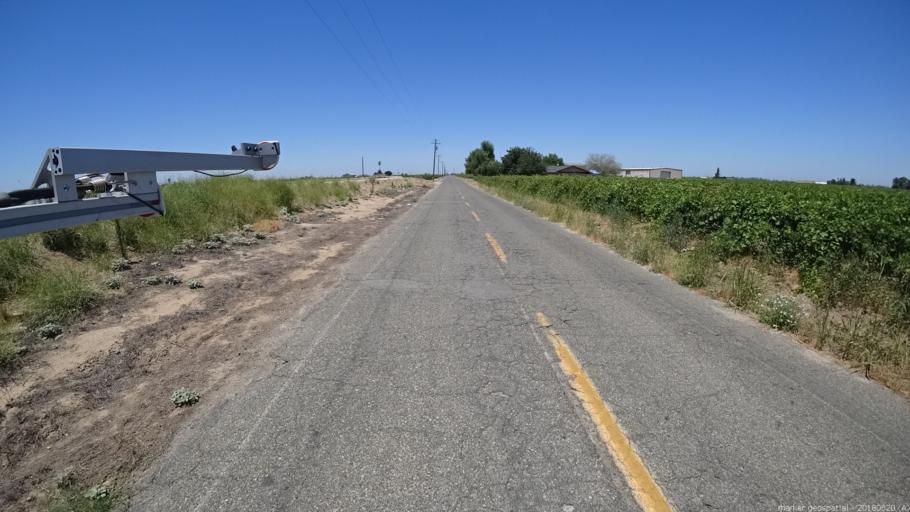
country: US
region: California
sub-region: Fresno County
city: Biola
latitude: 36.8658
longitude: -120.0138
